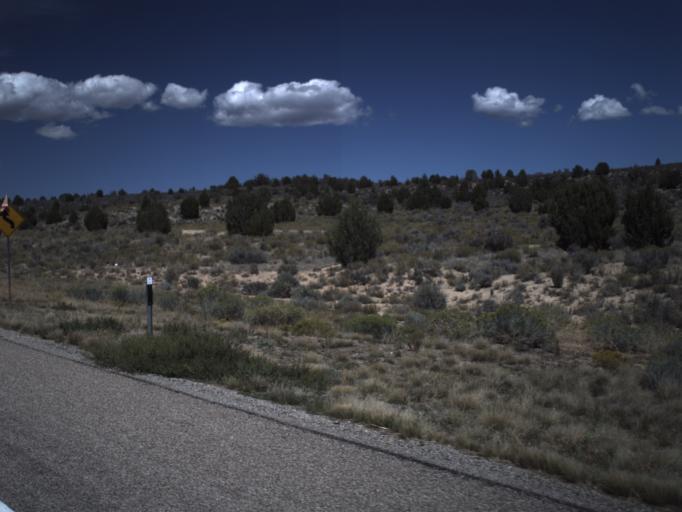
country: US
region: Utah
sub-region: Washington County
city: Ivins
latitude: 37.3150
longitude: -113.6774
